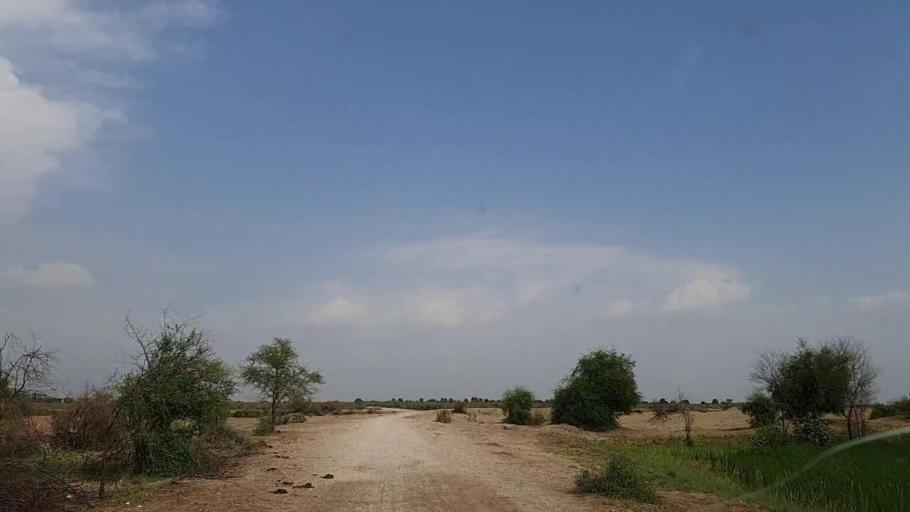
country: PK
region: Sindh
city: Khanpur
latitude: 27.8311
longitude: 69.5069
